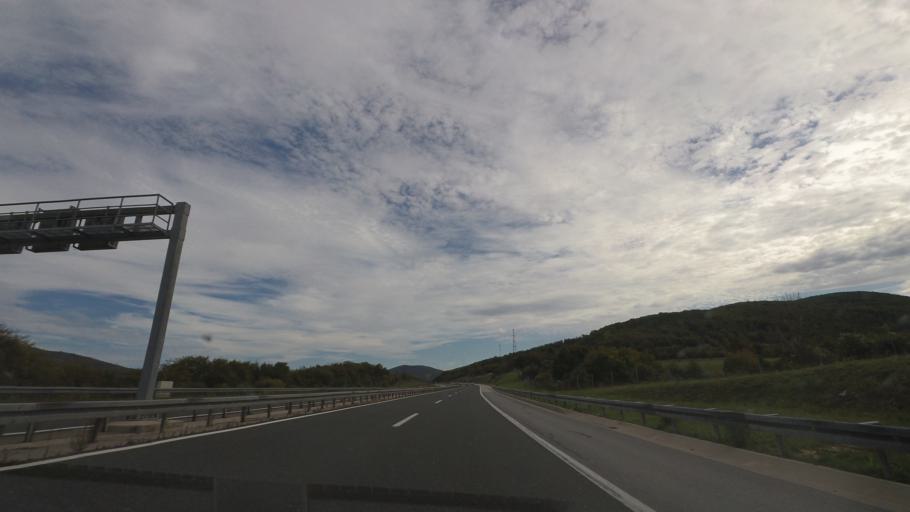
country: HR
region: Licko-Senjska
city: Brinje
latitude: 44.9459
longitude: 15.1609
